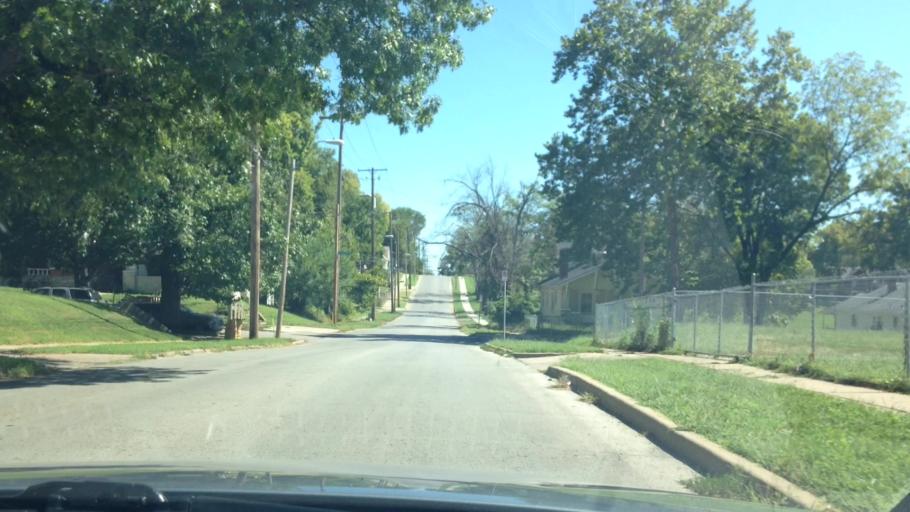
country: US
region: Missouri
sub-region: Jackson County
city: Kansas City
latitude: 39.0482
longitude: -94.5523
